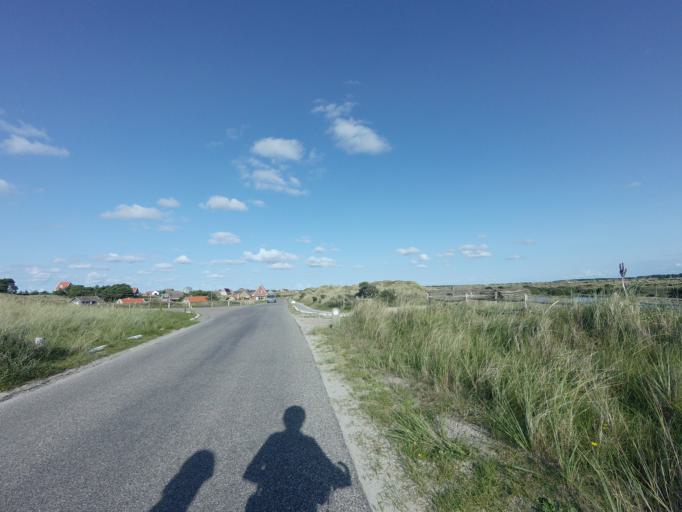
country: NL
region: Friesland
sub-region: Gemeente Terschelling
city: West-Terschelling
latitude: 53.3972
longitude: 5.2546
